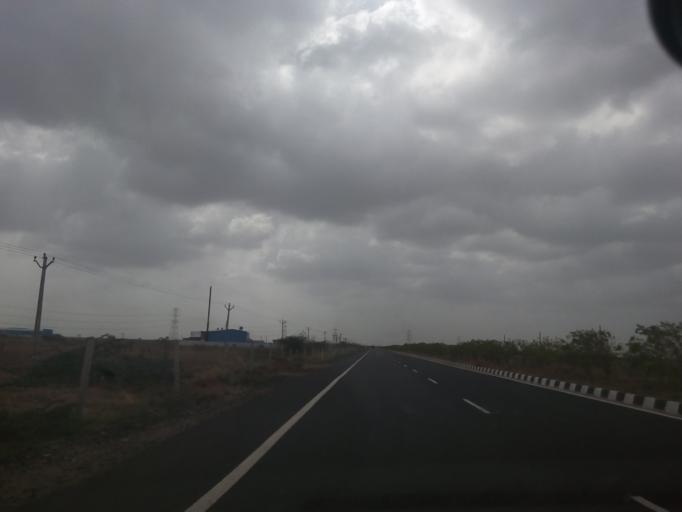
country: IN
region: Gujarat
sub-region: Rajkot
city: Morbi
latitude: 23.0503
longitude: 70.8733
